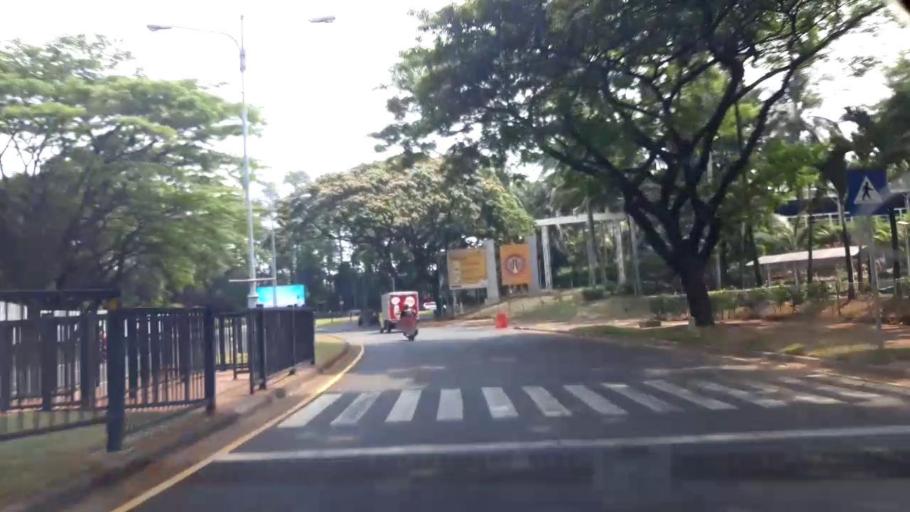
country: ID
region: Banten
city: Tangerang
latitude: -6.2260
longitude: 106.6047
